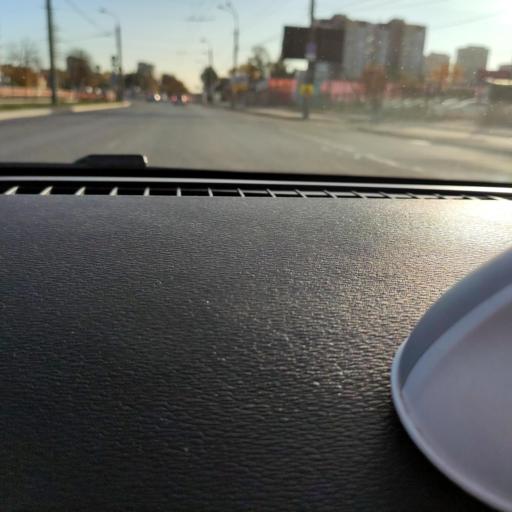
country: RU
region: Samara
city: Samara
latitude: 53.2115
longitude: 50.1991
